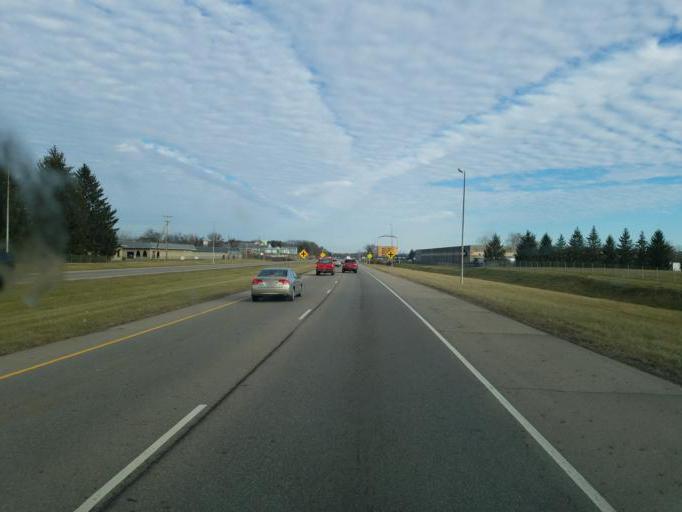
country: US
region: Ohio
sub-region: Licking County
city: Newark
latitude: 40.0629
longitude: -82.3608
